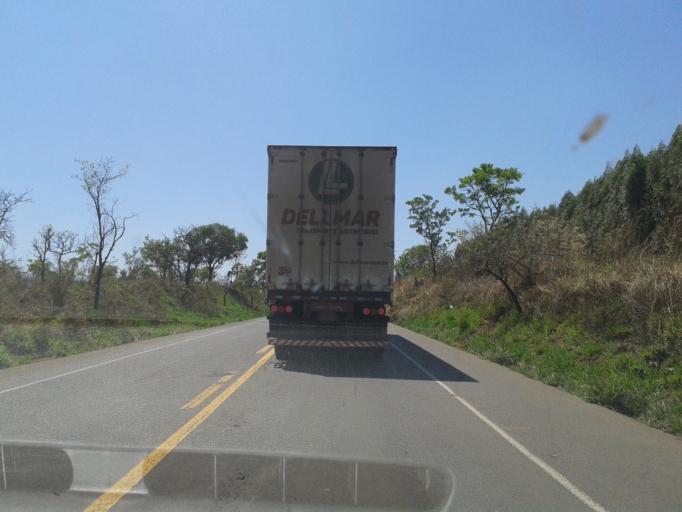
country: BR
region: Minas Gerais
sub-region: Araxa
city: Araxa
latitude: -19.4351
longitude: -47.2046
